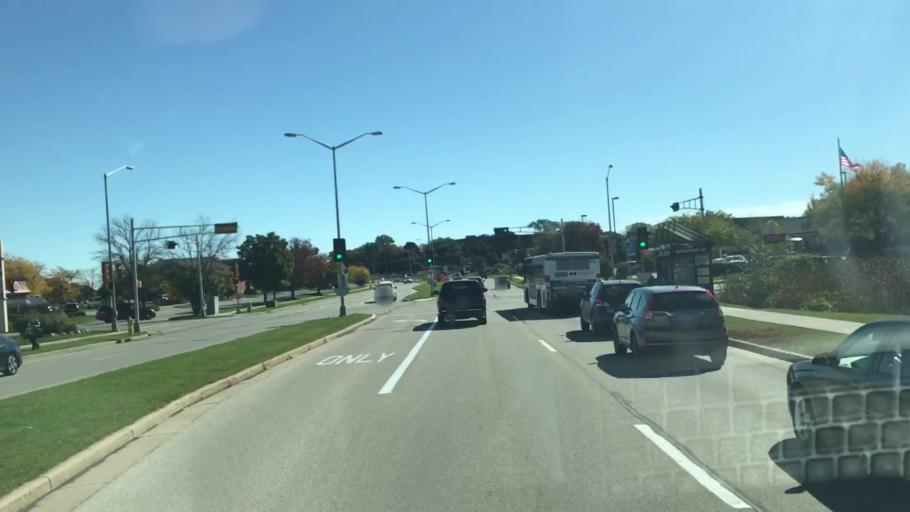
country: US
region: Wisconsin
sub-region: Waukesha County
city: Pewaukee
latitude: 43.0434
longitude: -88.2607
